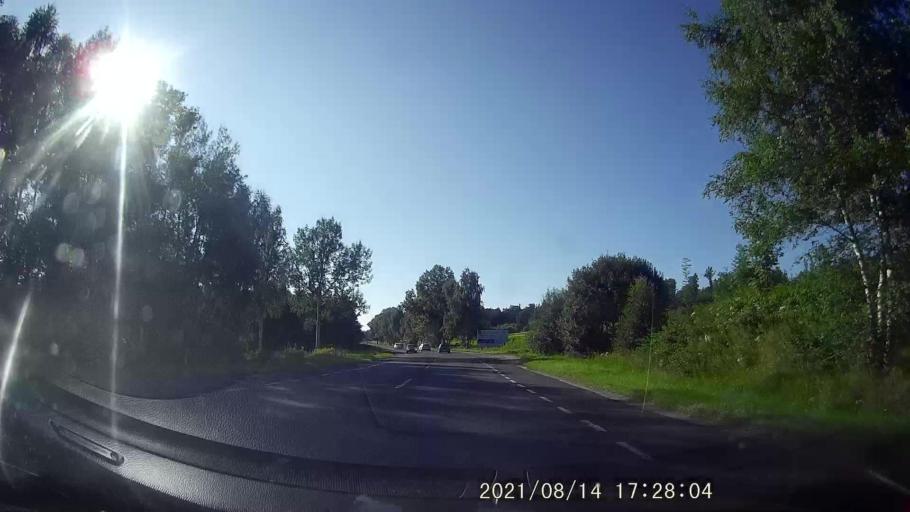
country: PL
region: Lower Silesian Voivodeship
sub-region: Jelenia Gora
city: Jelenia Gora
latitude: 50.9124
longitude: 15.6910
